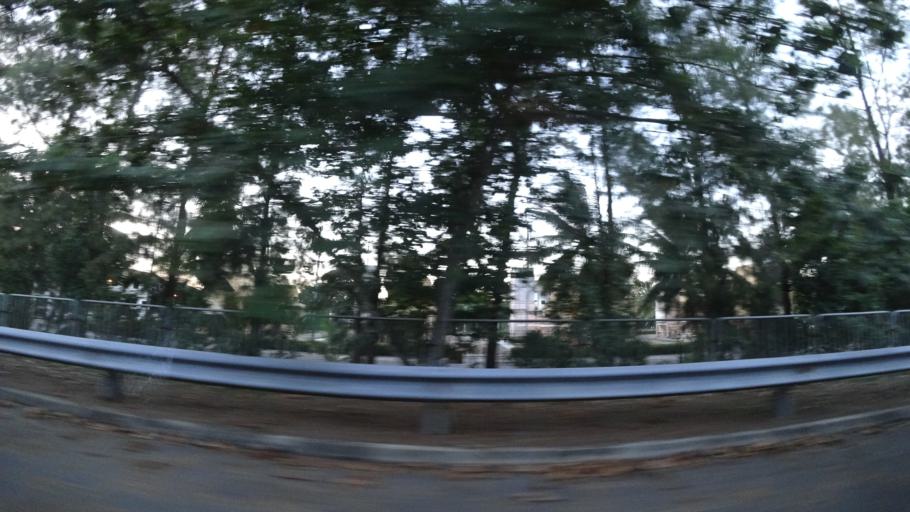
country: BN
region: Brunei and Muara
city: Bandar Seri Begawan
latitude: 4.9501
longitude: 114.8405
